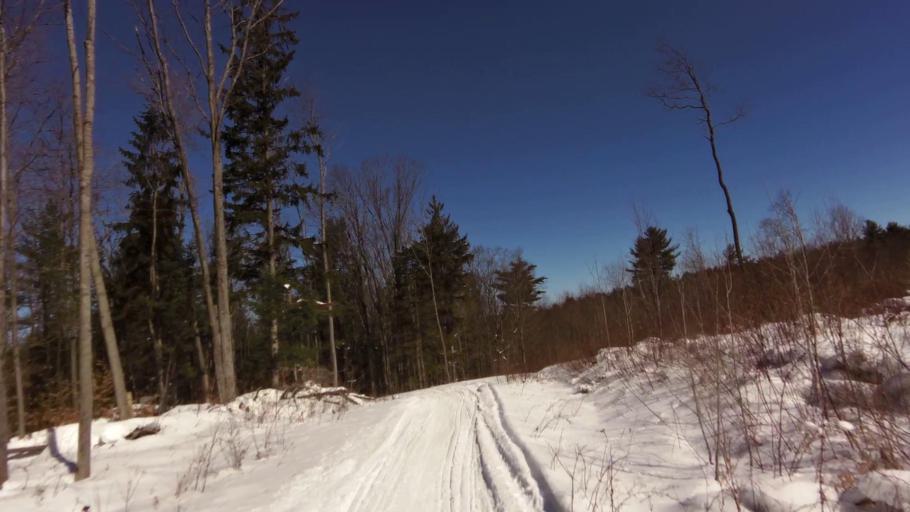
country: US
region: New York
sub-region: Allegany County
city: Cuba
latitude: 42.3006
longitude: -78.2409
